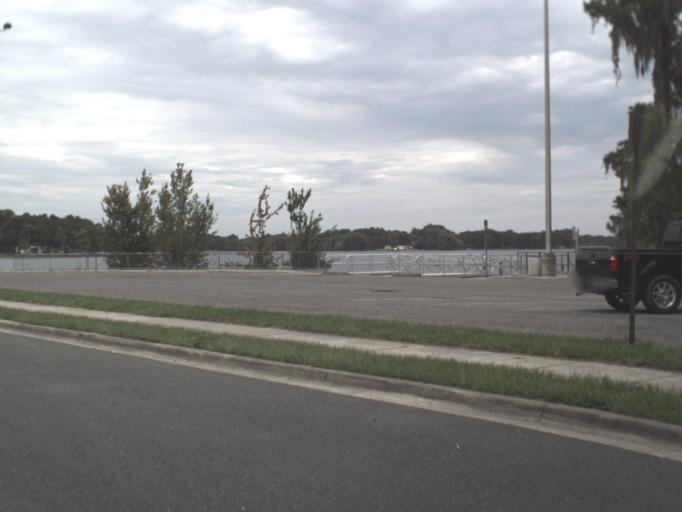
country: US
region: Florida
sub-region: Citrus County
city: Inverness
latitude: 28.8332
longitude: -82.3171
